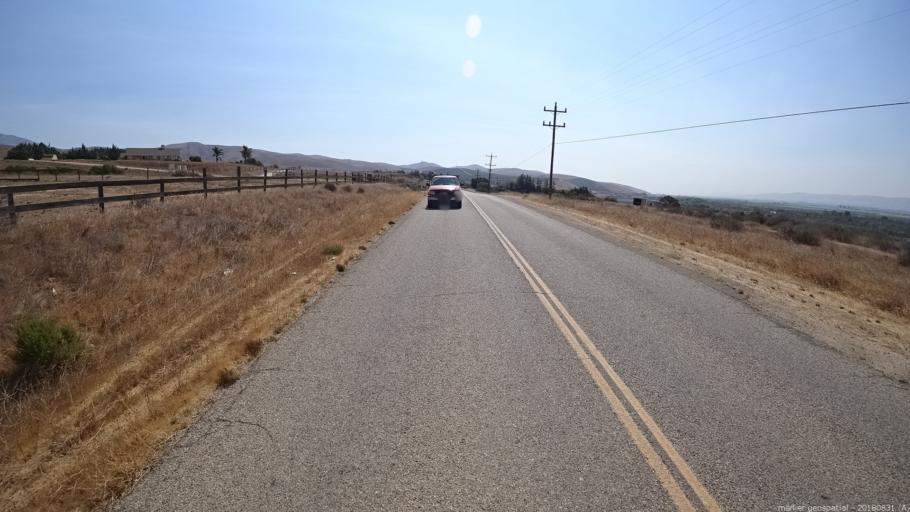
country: US
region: California
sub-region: Monterey County
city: Soledad
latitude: 36.4047
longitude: -121.2604
